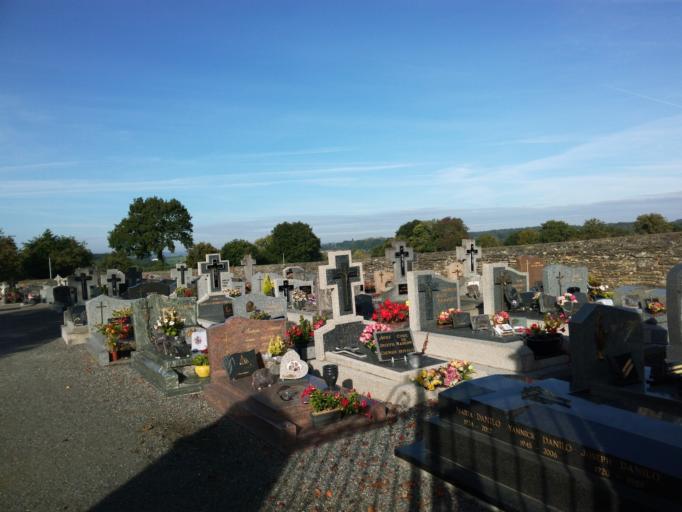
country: FR
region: Brittany
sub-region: Departement du Morbihan
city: Peillac
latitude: 47.7415
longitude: -2.2140
